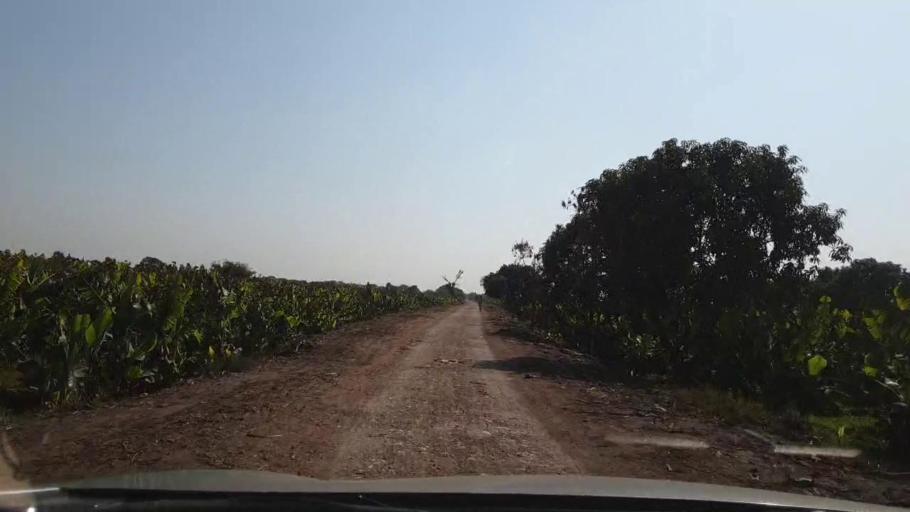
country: PK
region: Sindh
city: Mirpur Khas
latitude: 25.5991
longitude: 68.8673
